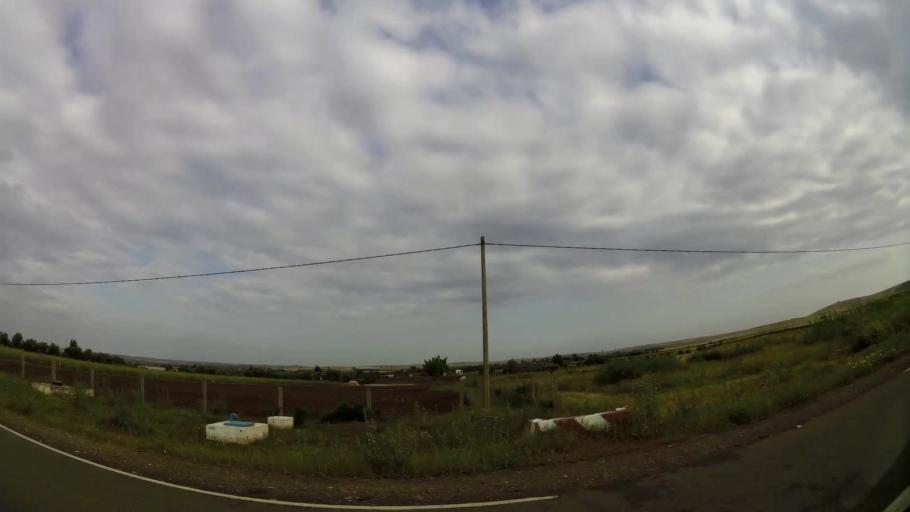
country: MA
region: Rabat-Sale-Zemmour-Zaer
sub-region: Khemisset
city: Khemisset
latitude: 33.7635
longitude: -6.1742
